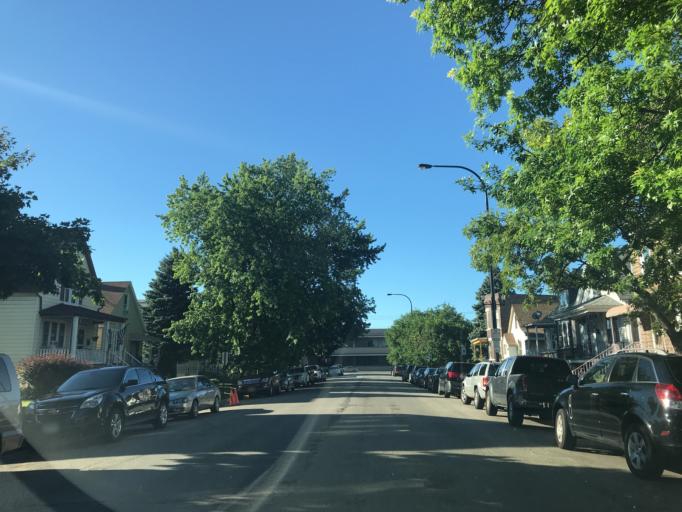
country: US
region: Illinois
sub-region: Cook County
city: Cicero
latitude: 41.8642
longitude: -87.7496
